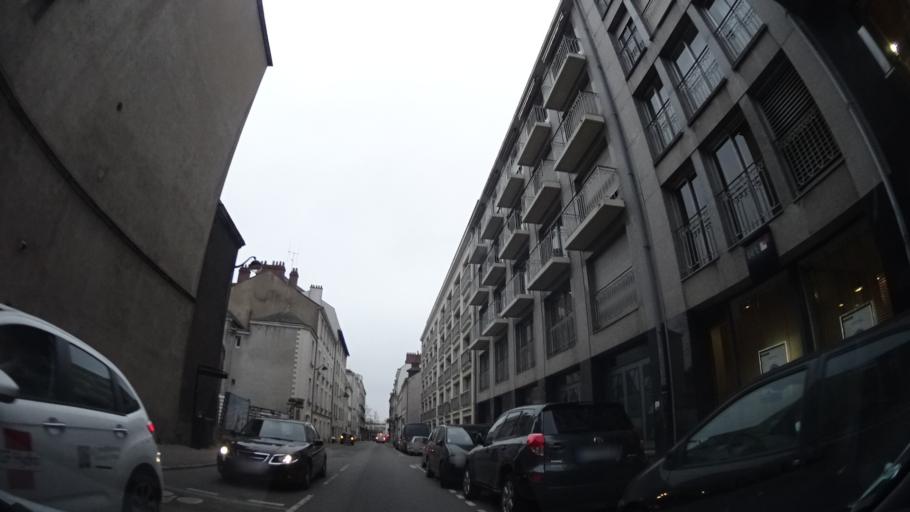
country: FR
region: Pays de la Loire
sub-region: Departement de la Loire-Atlantique
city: Nantes
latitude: 47.2162
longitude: -1.5659
